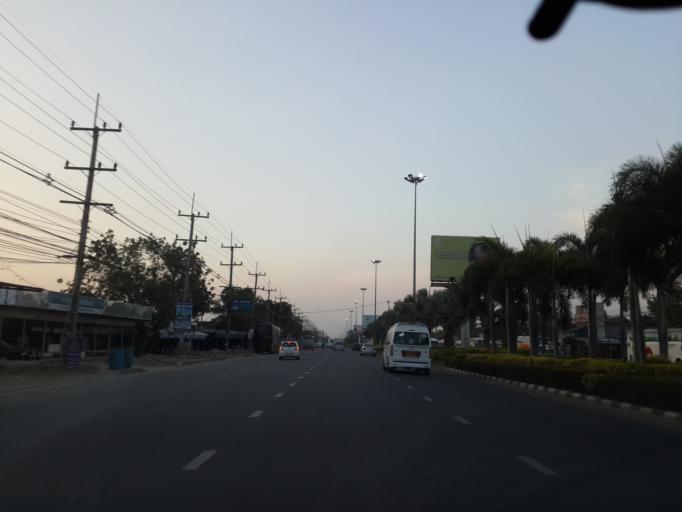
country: TH
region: Chon Buri
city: Phatthaya
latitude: 12.8662
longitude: 100.9049
